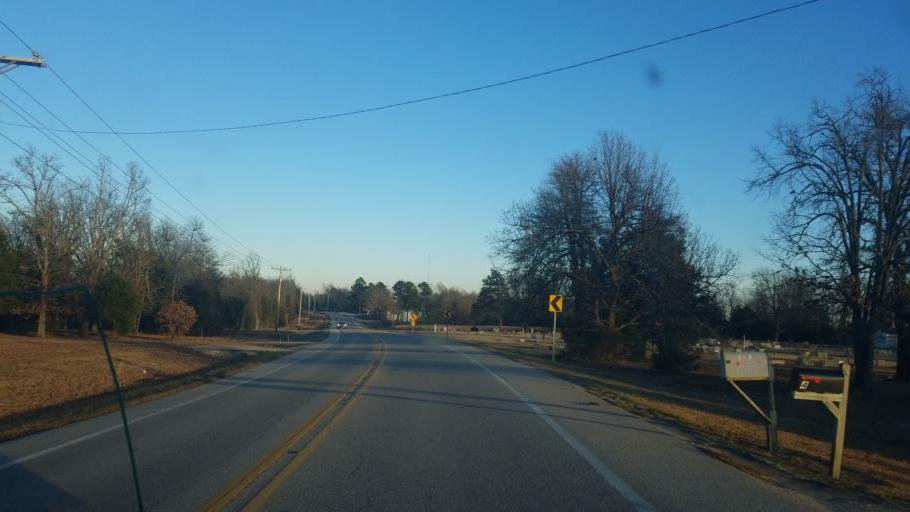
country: US
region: Arkansas
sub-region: Baxter County
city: Mountain Home
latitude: 36.3838
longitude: -92.1726
